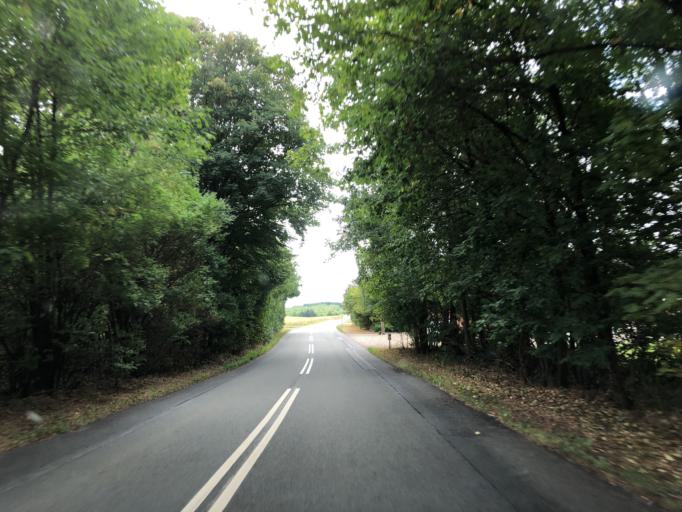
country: DK
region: South Denmark
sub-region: Vejle Kommune
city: Egtved
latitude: 55.6367
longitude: 9.1976
